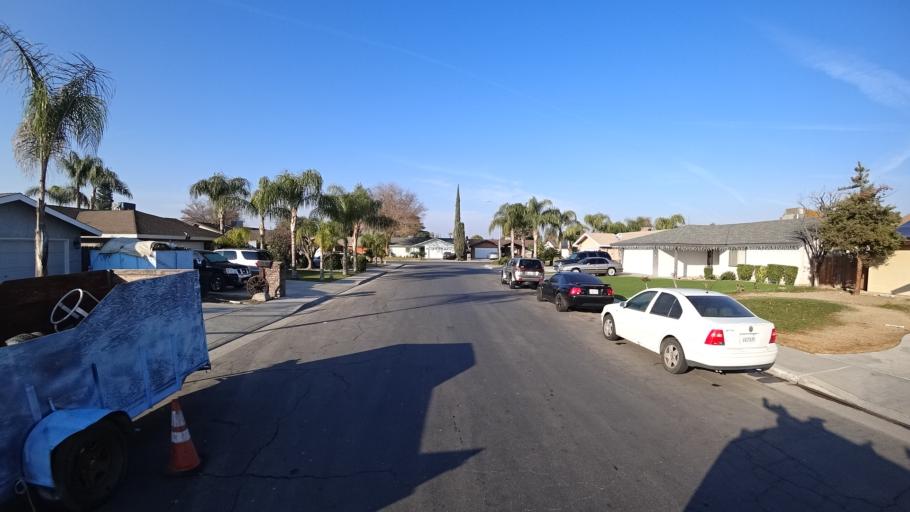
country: US
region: California
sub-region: Kern County
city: Greenfield
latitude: 35.3004
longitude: -119.0229
